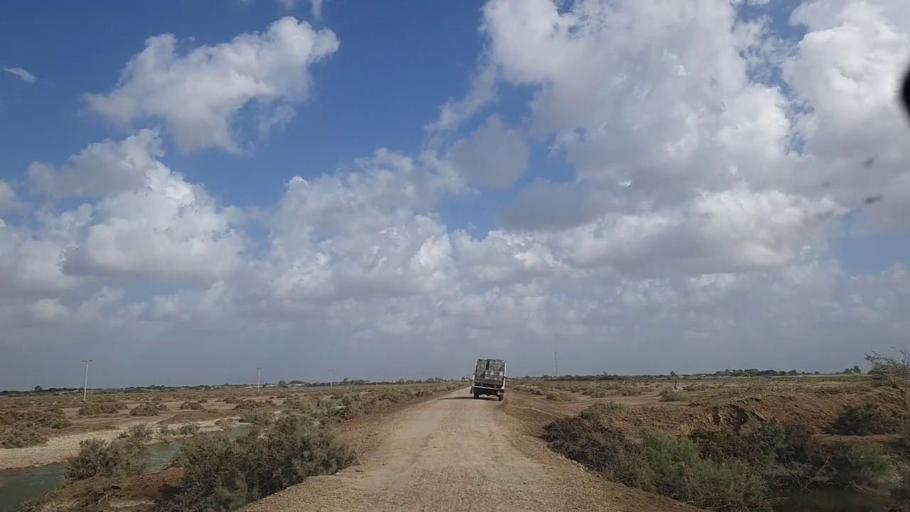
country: PK
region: Sindh
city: Keti Bandar
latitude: 24.1061
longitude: 67.5891
